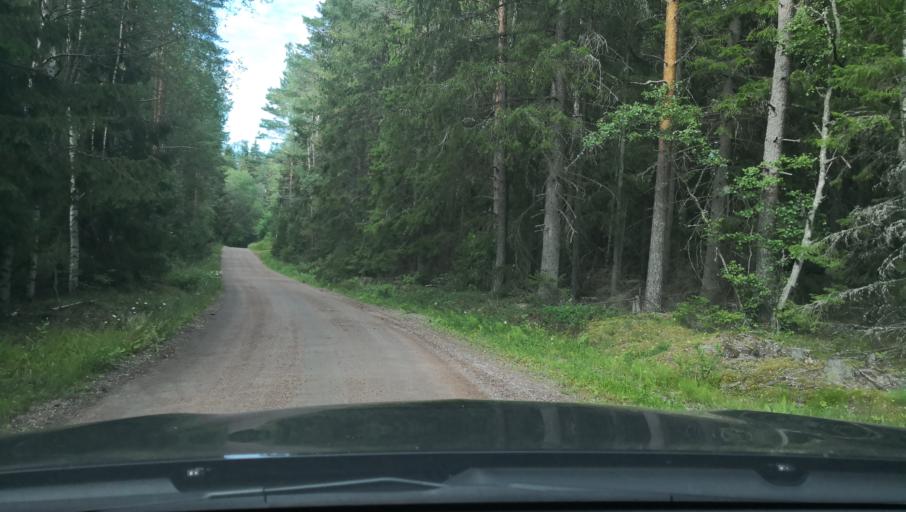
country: SE
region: Vaestmanland
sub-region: Surahammars Kommun
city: Surahammar
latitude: 59.6592
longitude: 16.1548
